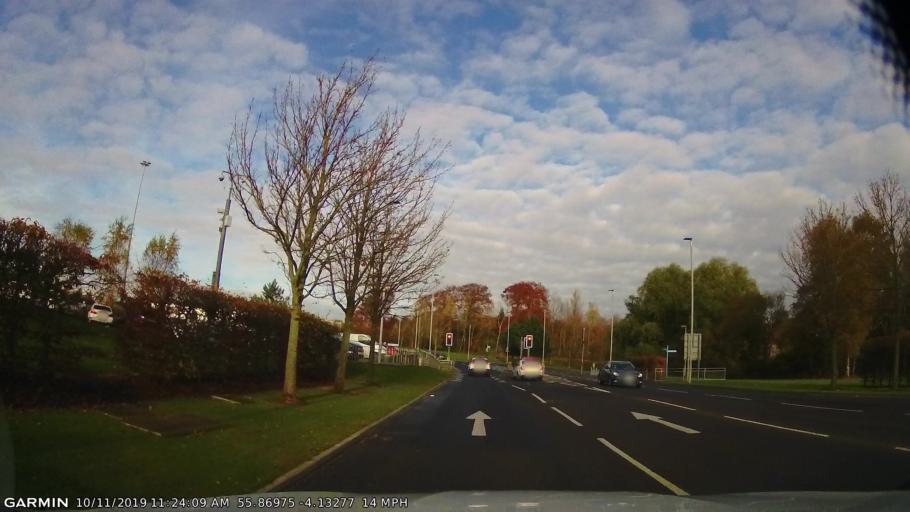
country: GB
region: Scotland
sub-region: North Lanarkshire
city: Stepps
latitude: 55.8697
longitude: -4.1328
